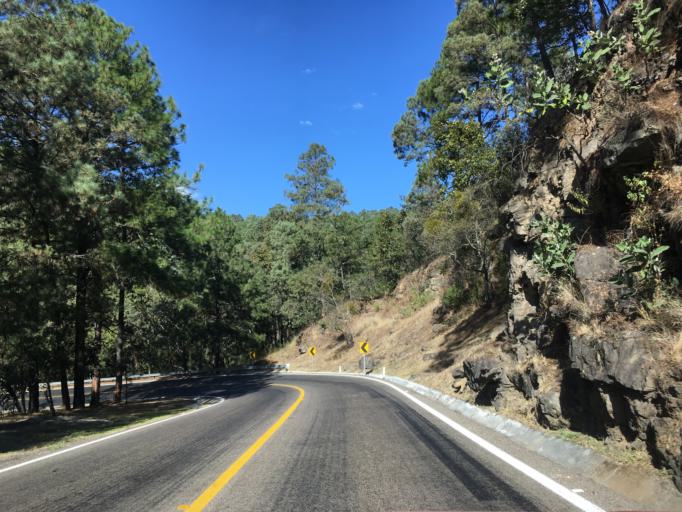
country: MX
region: Michoacan
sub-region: Hidalgo
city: Tierras Coloradas (San Pedro)
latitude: 19.6660
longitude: -100.7215
